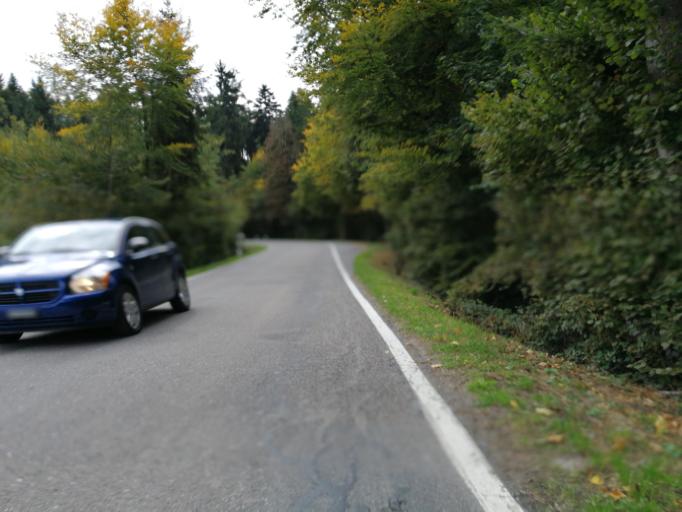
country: CH
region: Zurich
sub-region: Bezirk Meilen
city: Dorf
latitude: 47.2569
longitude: 8.7416
